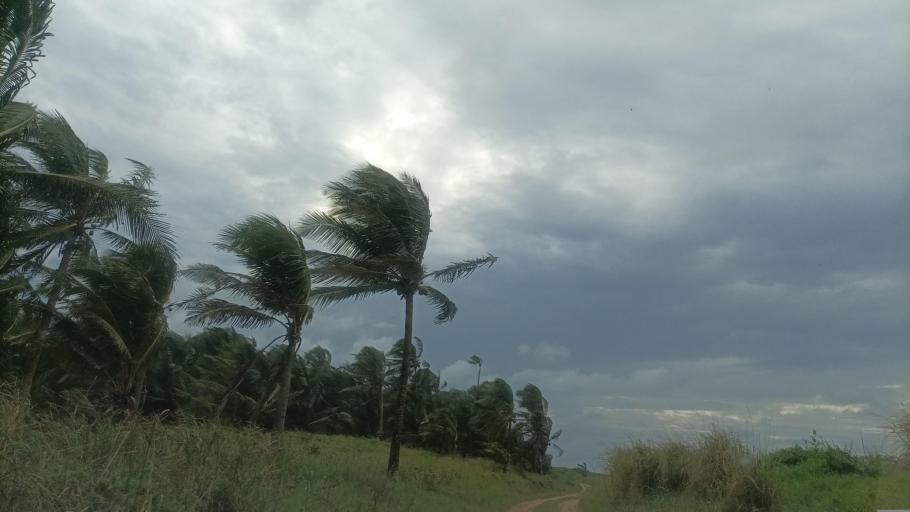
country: MX
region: Veracruz
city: Agua Dulce
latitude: 18.1817
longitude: -94.2647
